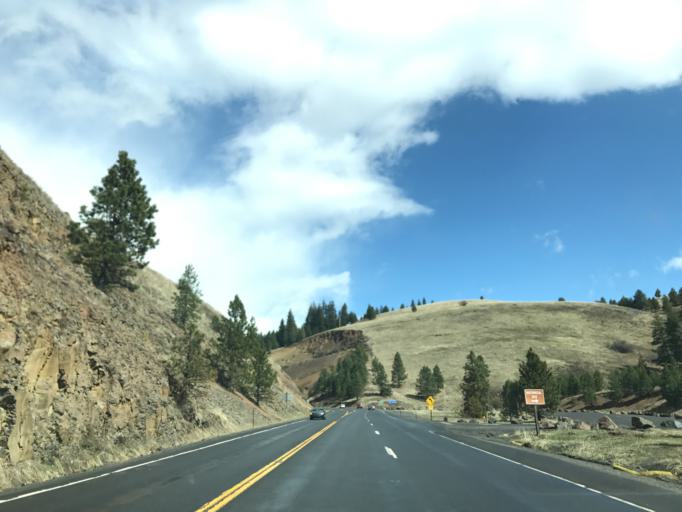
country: US
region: Idaho
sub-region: Idaho County
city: Grangeville
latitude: 45.8387
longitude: -116.2385
